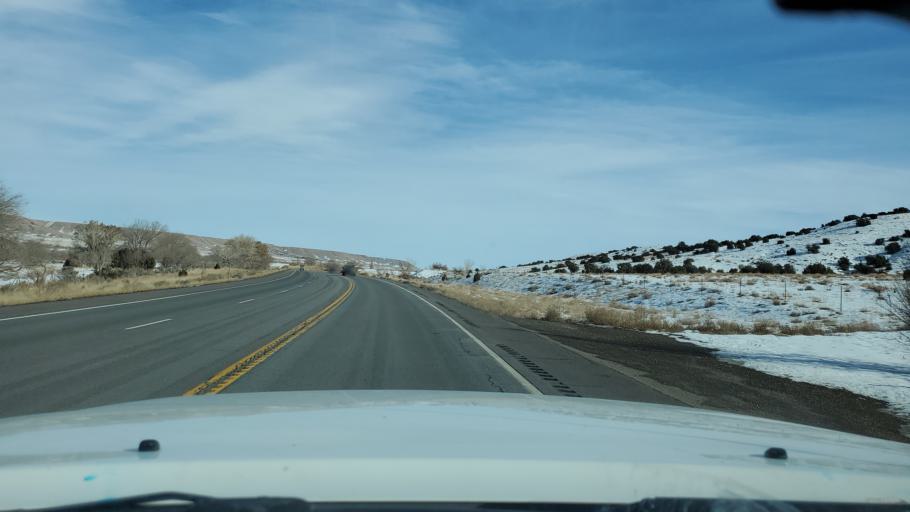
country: US
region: Utah
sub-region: Duchesne County
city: Duchesne
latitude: 40.1688
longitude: -110.3139
